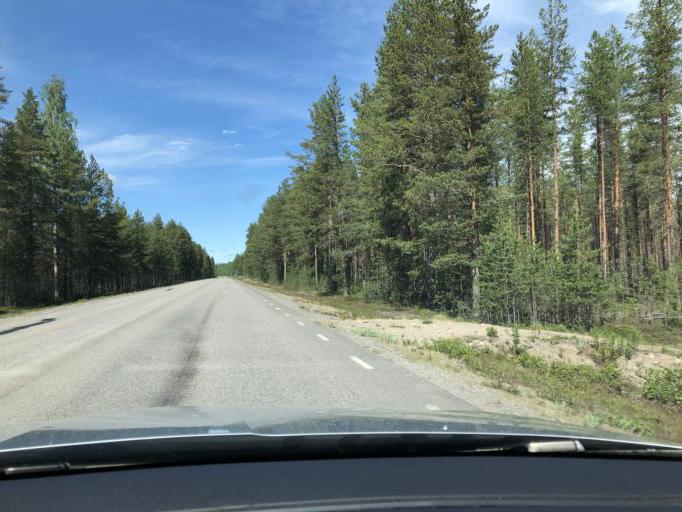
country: SE
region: Norrbotten
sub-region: Pitea Kommun
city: Bergsviken
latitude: 65.3771
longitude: 21.3461
